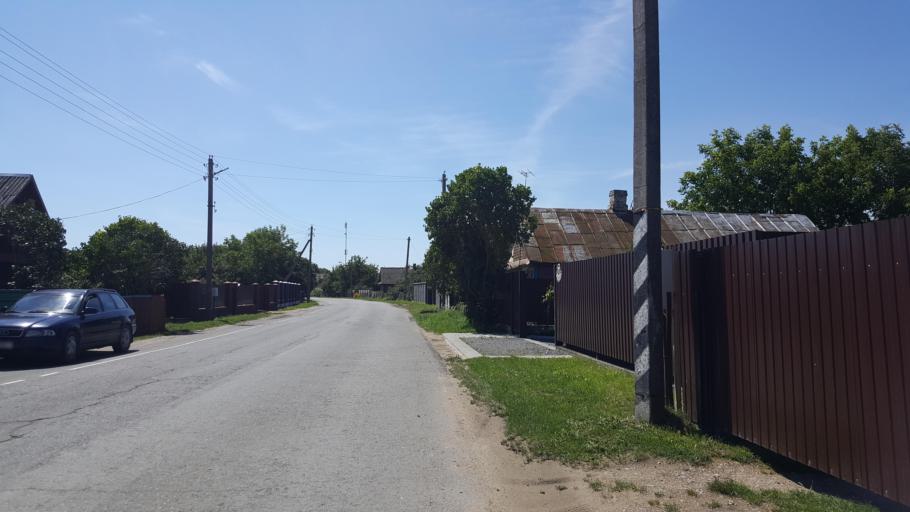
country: BY
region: Brest
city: Charnawchytsy
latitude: 52.2232
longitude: 23.7388
